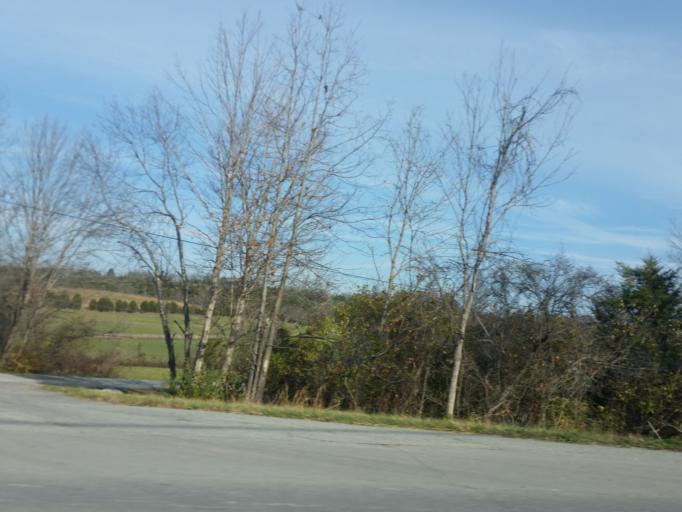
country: US
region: Kentucky
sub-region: Campbell County
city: Claryville
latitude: 38.8352
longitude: -84.3673
